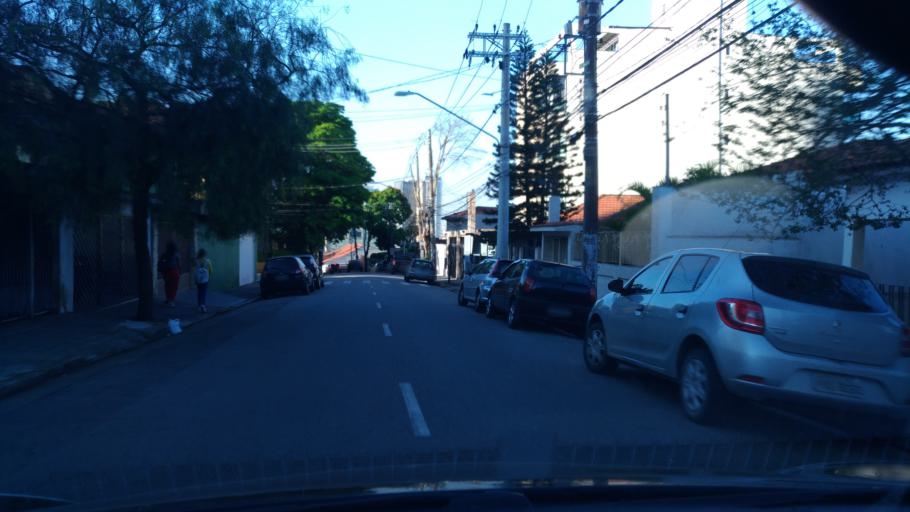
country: BR
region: Sao Paulo
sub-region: Sao Bernardo Do Campo
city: Sao Bernardo do Campo
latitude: -23.7010
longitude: -46.5548
